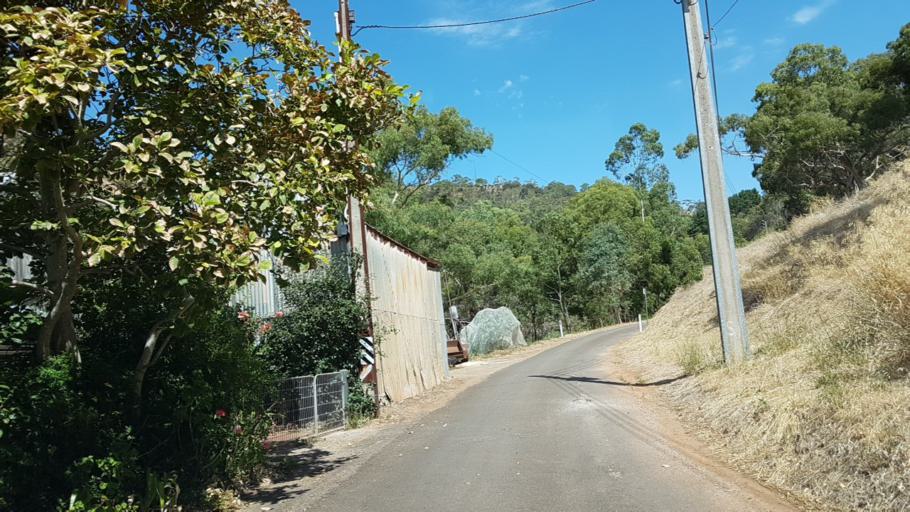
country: AU
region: South Australia
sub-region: Burnside
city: Mount Osmond
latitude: -34.9919
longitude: 138.6546
